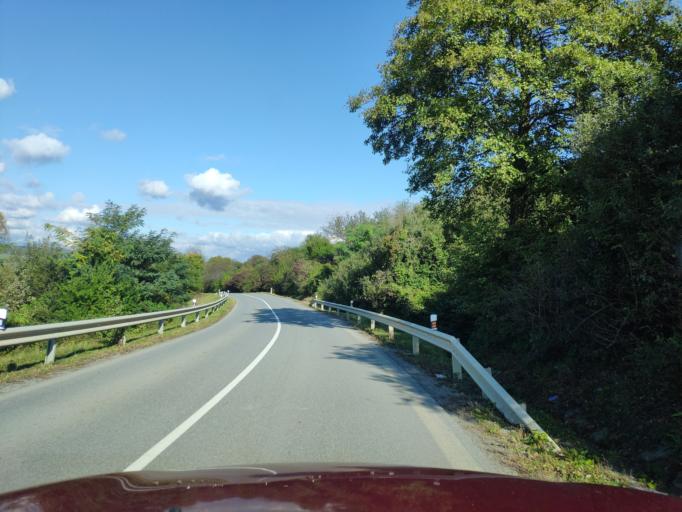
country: SK
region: Presovsky
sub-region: Okres Presov
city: Presov
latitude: 48.8868
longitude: 21.2637
